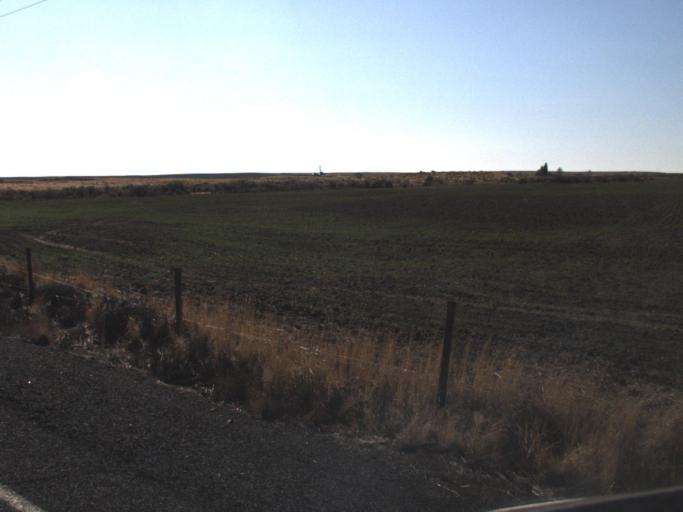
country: US
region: Washington
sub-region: Franklin County
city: Connell
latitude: 46.7785
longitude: -118.5474
